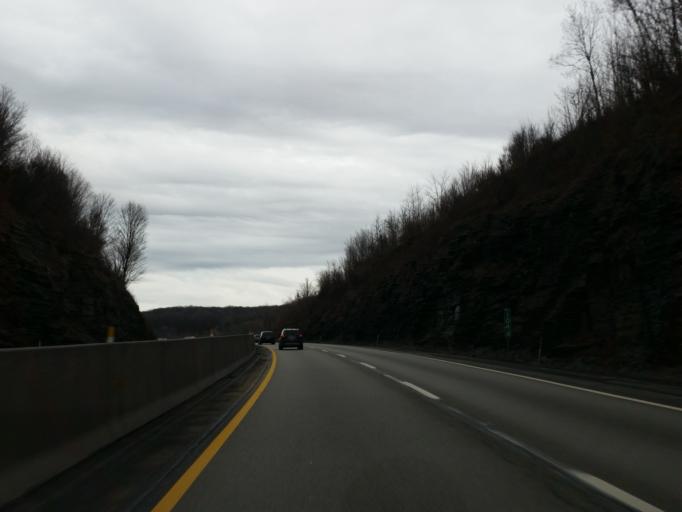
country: US
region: Pennsylvania
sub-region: Somerset County
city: Somerset
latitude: 40.0692
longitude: -79.1572
